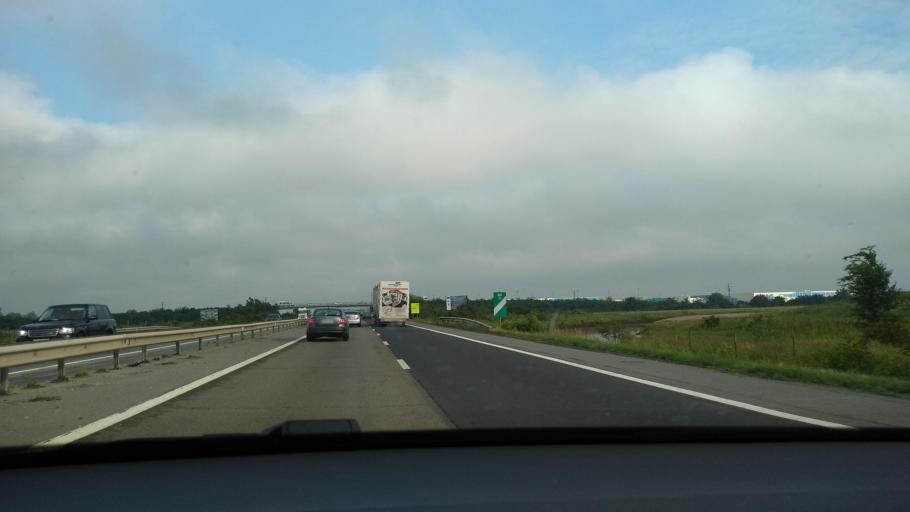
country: RO
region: Giurgiu
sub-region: Comuna Bolintin Deal
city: Bolintin Deal
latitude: 44.4632
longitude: 25.8487
